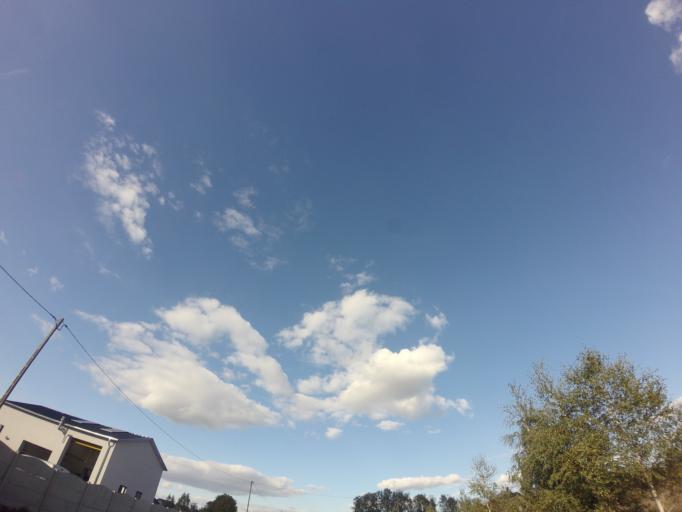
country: PL
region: Greater Poland Voivodeship
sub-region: Powiat nowotomyski
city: Nowy Tomysl
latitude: 52.2573
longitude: 16.1346
